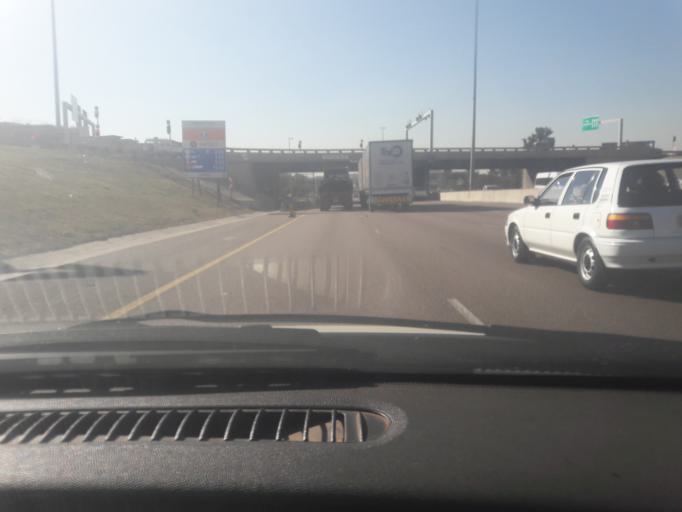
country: ZA
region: Gauteng
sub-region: City of Tshwane Metropolitan Municipality
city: Pretoria
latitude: -25.7856
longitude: 28.2700
